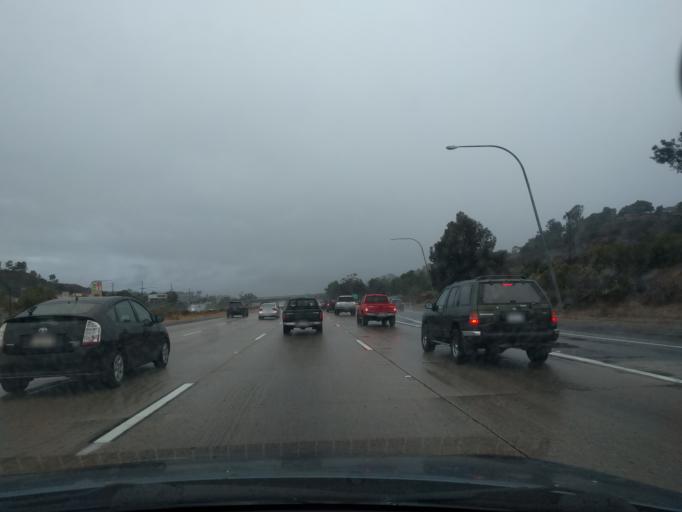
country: US
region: California
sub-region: San Diego County
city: La Mesa
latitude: 32.8059
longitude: -117.1131
